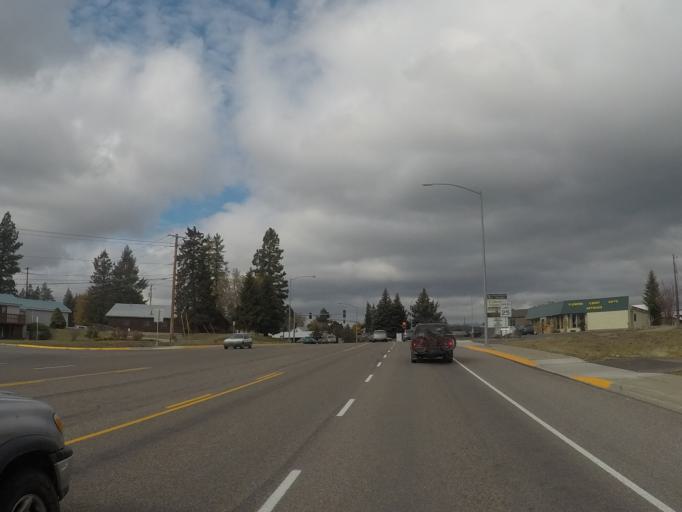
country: US
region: Montana
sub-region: Flathead County
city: Columbia Falls
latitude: 48.3687
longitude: -114.1796
